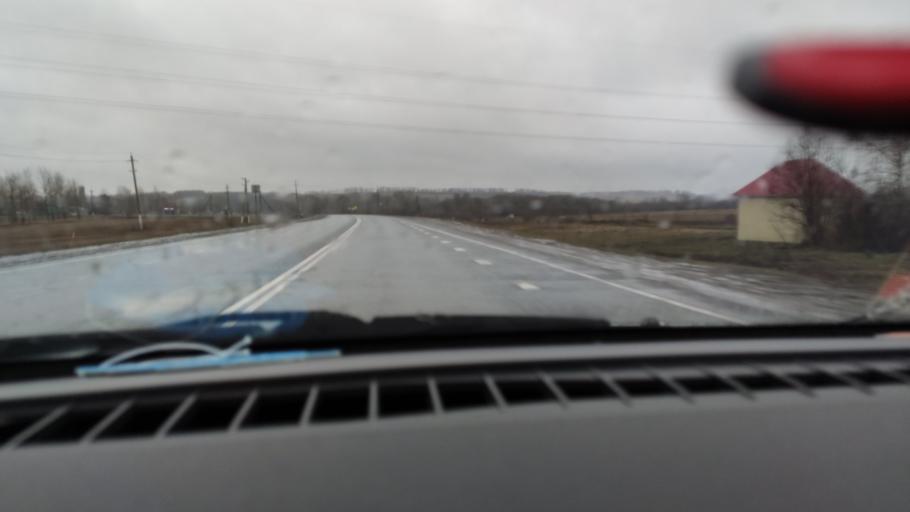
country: RU
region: Tatarstan
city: Mendeleyevsk
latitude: 55.8629
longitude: 52.2134
